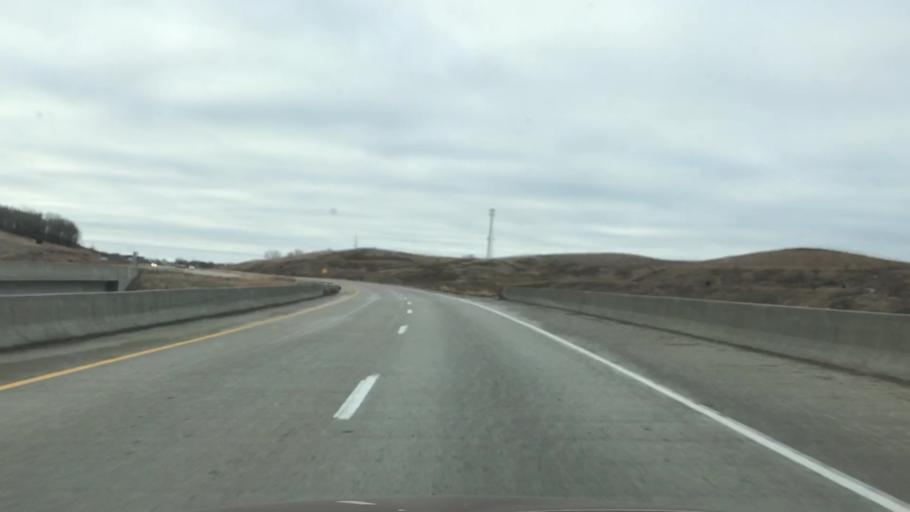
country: US
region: Iowa
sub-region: Woodbury County
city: Sioux City
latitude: 42.5188
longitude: -96.3390
